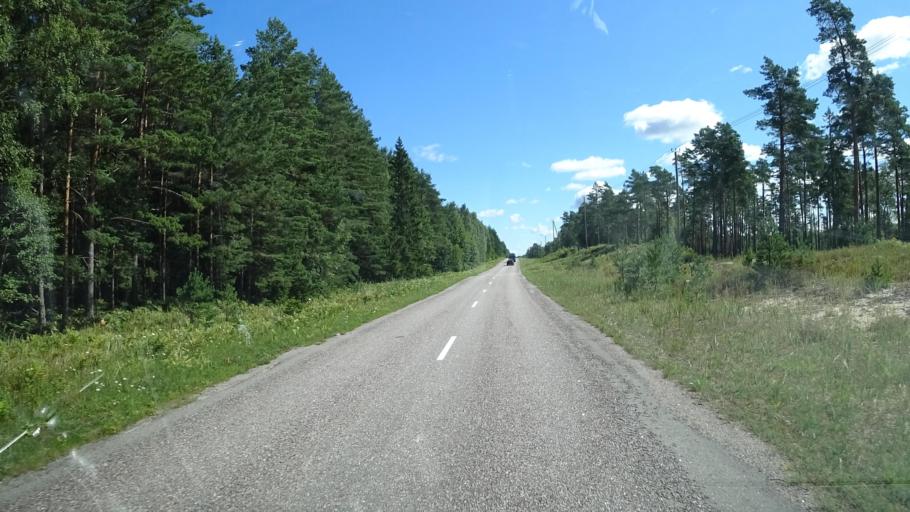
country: LV
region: Ventspils
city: Ventspils
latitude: 57.5593
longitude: 21.7825
